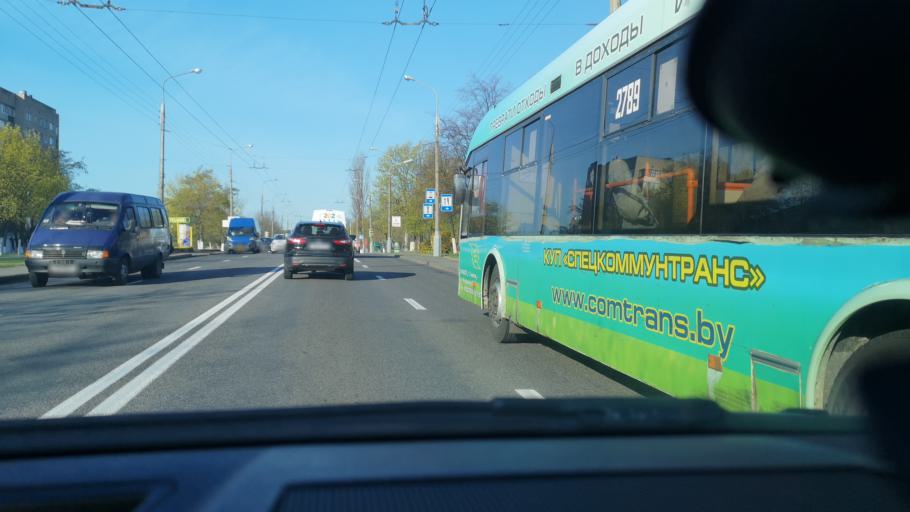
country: BY
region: Gomel
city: Gomel
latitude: 52.4154
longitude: 30.9595
